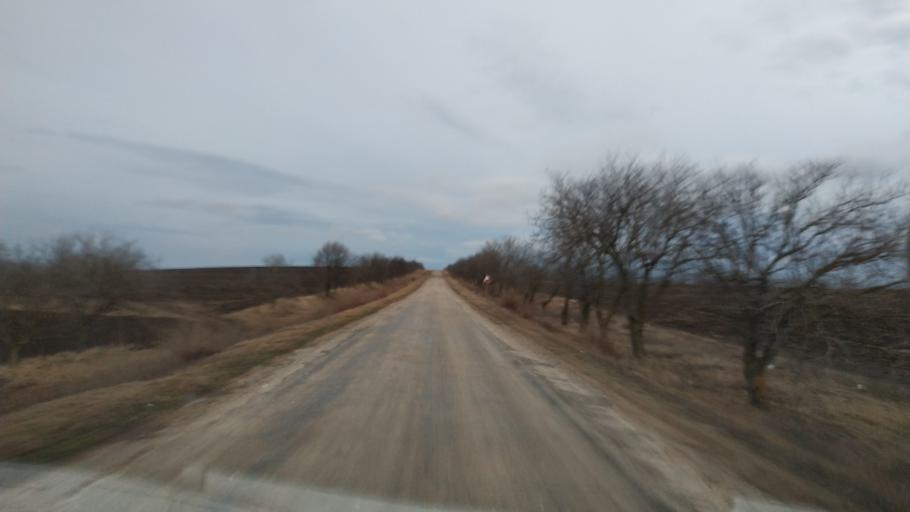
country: MD
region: Causeni
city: Causeni
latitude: 46.5798
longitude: 29.3912
